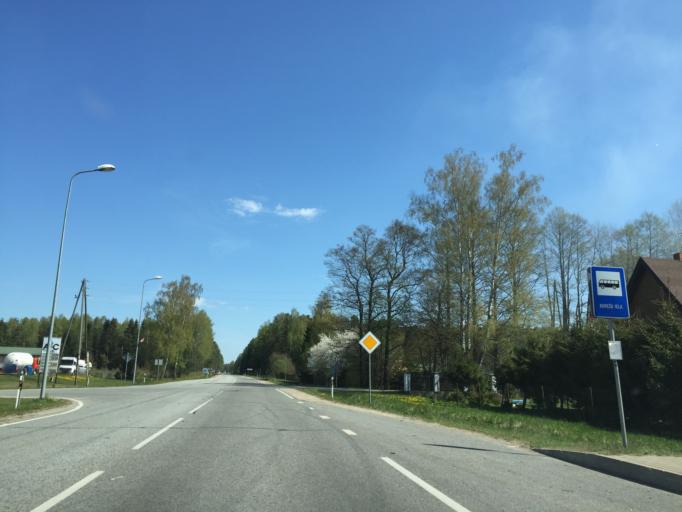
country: LV
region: Saulkrastu
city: Saulkrasti
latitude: 57.3211
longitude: 24.4249
